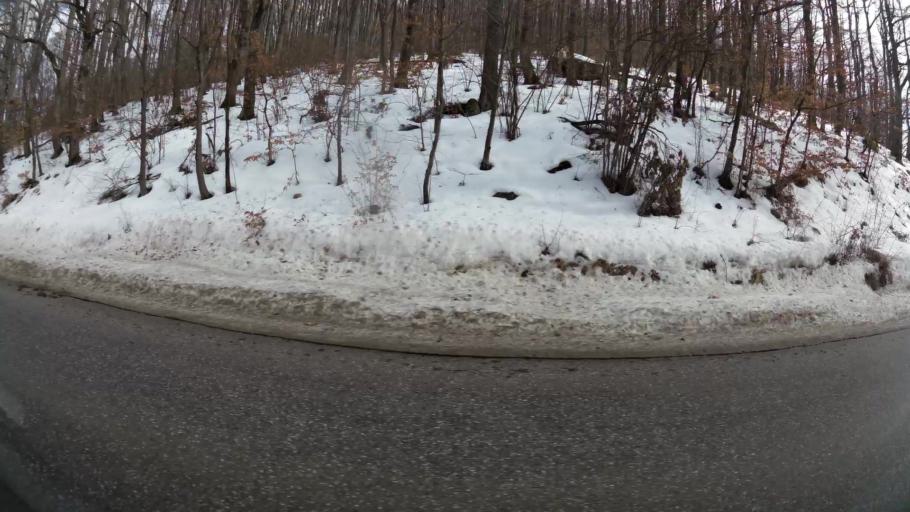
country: BG
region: Sofia-Capital
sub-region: Stolichna Obshtina
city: Sofia
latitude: 42.6344
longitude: 23.2257
